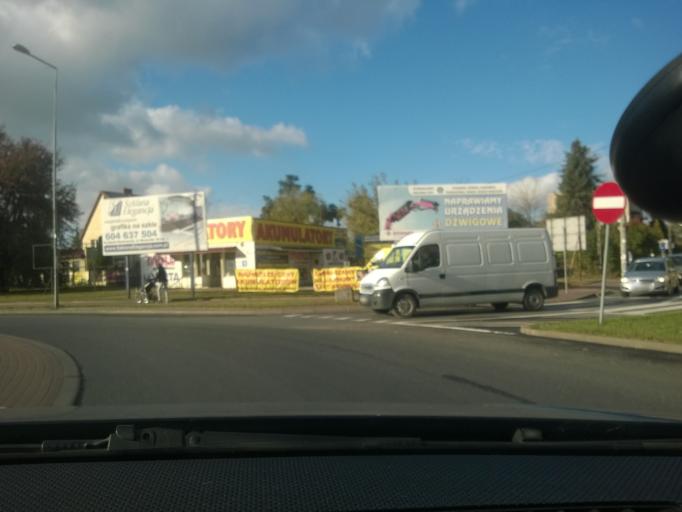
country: PL
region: Masovian Voivodeship
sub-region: Powiat pruszkowski
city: Pruszkow
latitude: 52.1726
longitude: 20.8033
